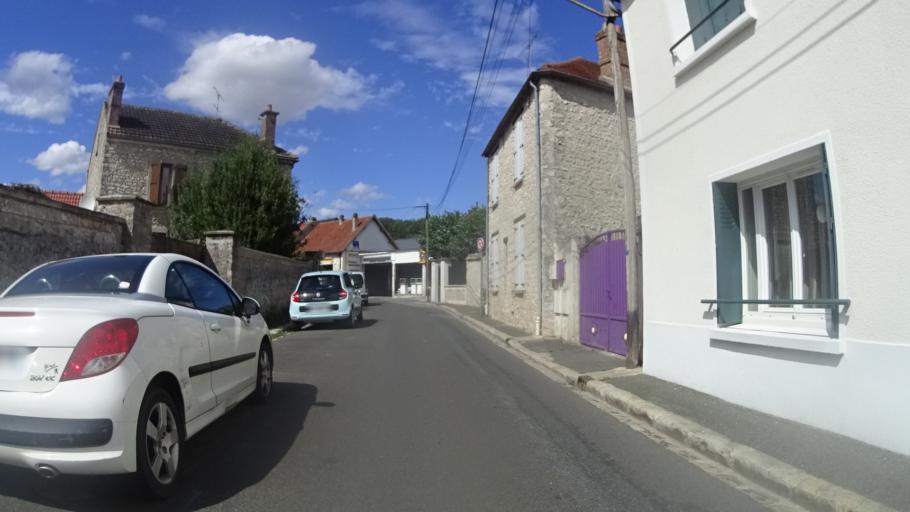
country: FR
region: Ile-de-France
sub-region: Departement de l'Essonne
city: Boutigny-sur-Essonne
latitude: 48.4349
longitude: 2.3779
